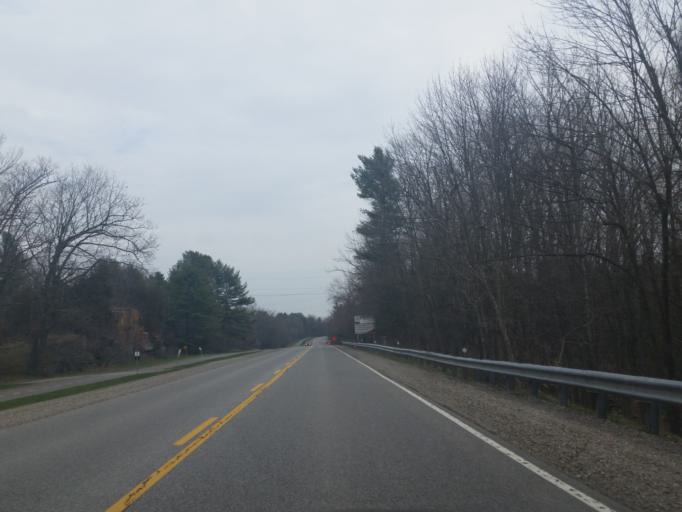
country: US
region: New York
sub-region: Jefferson County
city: Alexandria Bay
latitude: 44.3678
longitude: -75.9972
